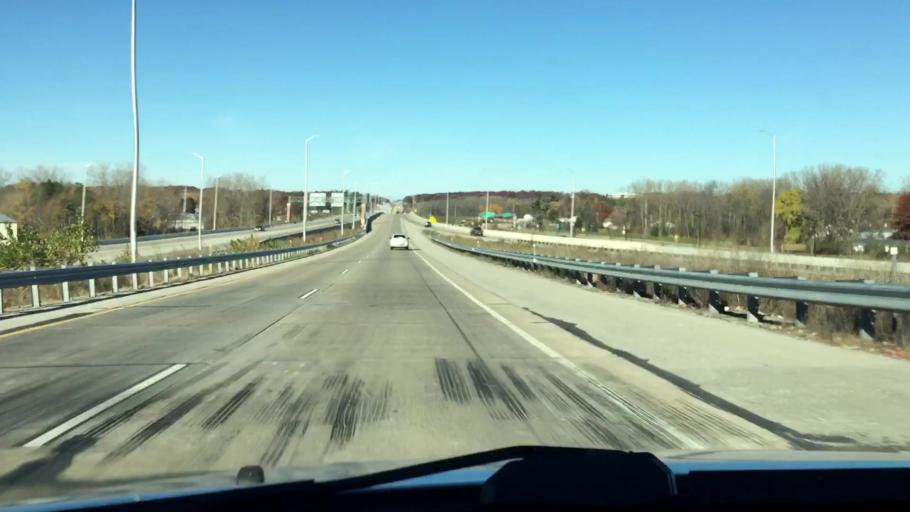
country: US
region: Wisconsin
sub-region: Brown County
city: Howard
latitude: 44.5404
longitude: -88.0815
